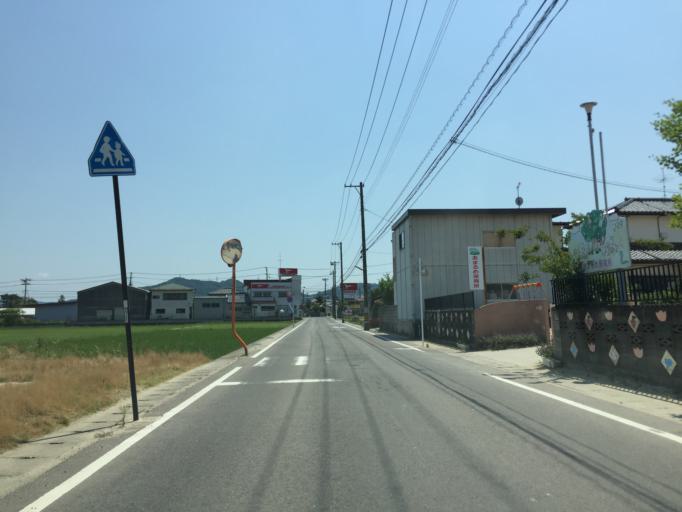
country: JP
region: Fukushima
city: Fukushima-shi
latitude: 37.8040
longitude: 140.4735
